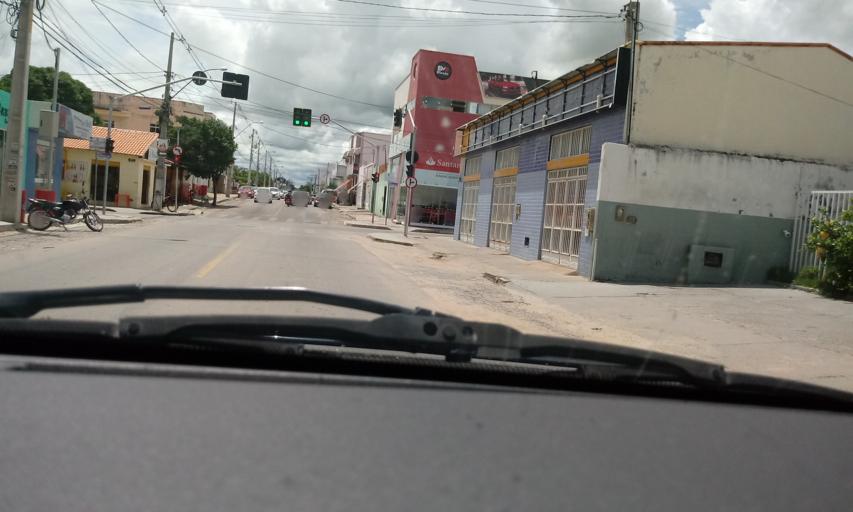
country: BR
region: Bahia
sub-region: Guanambi
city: Guanambi
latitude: -14.2170
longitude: -42.7737
